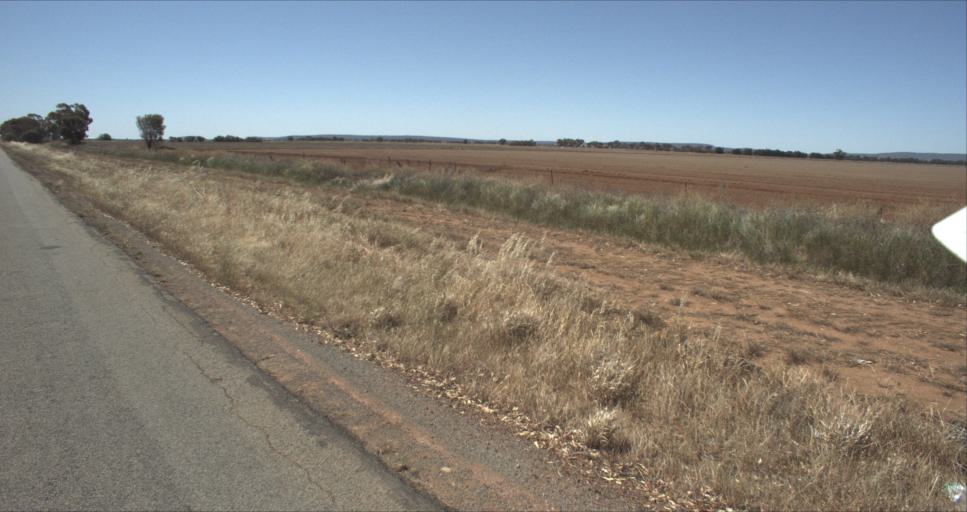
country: AU
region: New South Wales
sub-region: Leeton
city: Leeton
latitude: -34.5178
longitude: 146.3454
